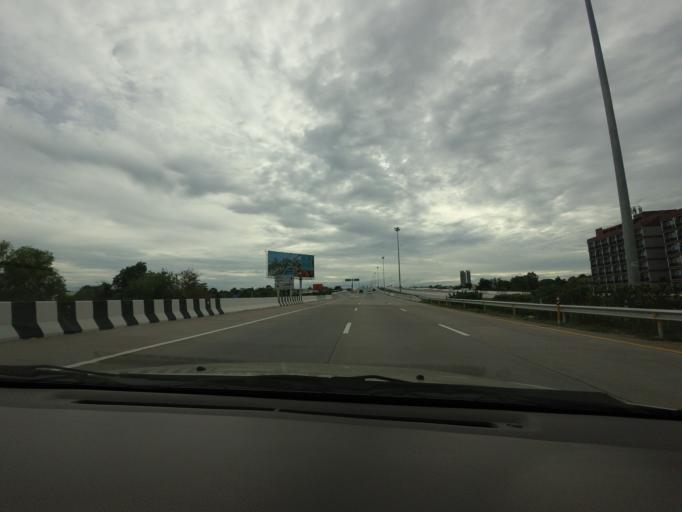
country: TH
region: Chon Buri
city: Phatthaya
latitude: 12.9432
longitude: 100.9156
